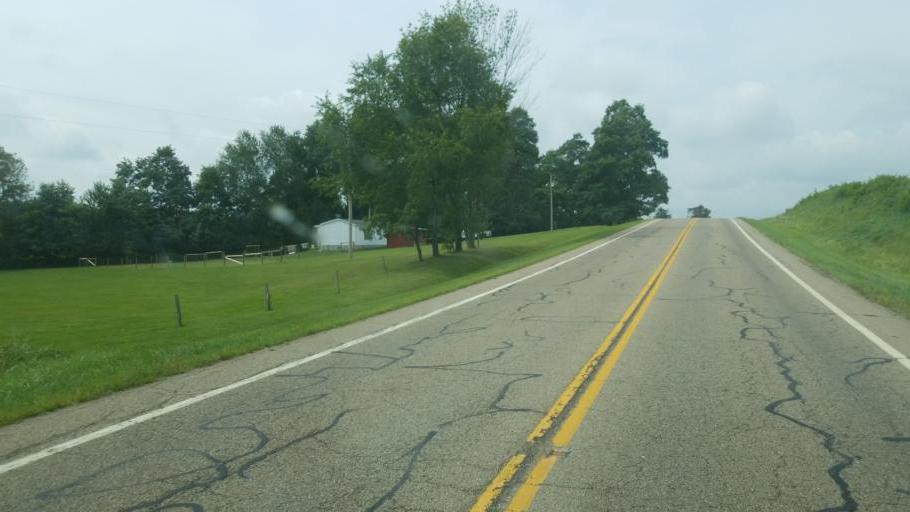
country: US
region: Ohio
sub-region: Knox County
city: Danville
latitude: 40.4985
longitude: -82.3421
